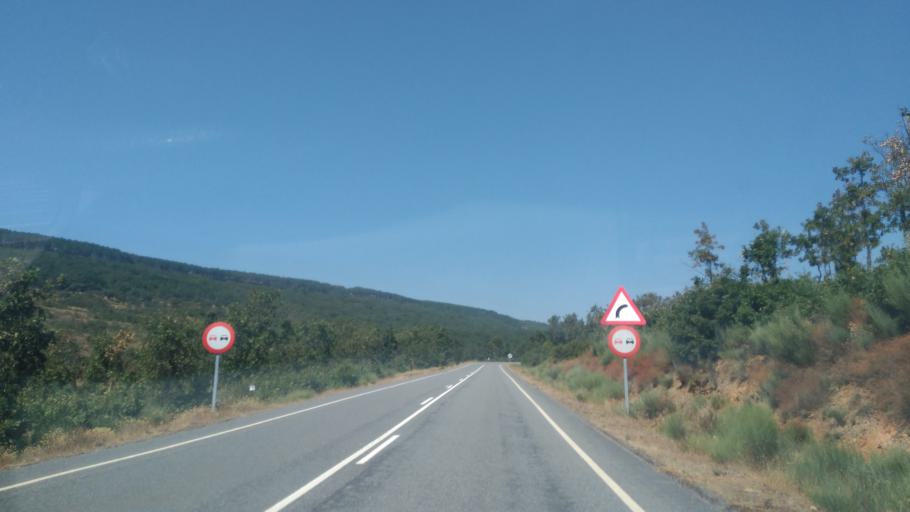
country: ES
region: Castille and Leon
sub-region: Provincia de Salamanca
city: Cereceda de la Sierra
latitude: 40.5811
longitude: -6.0803
